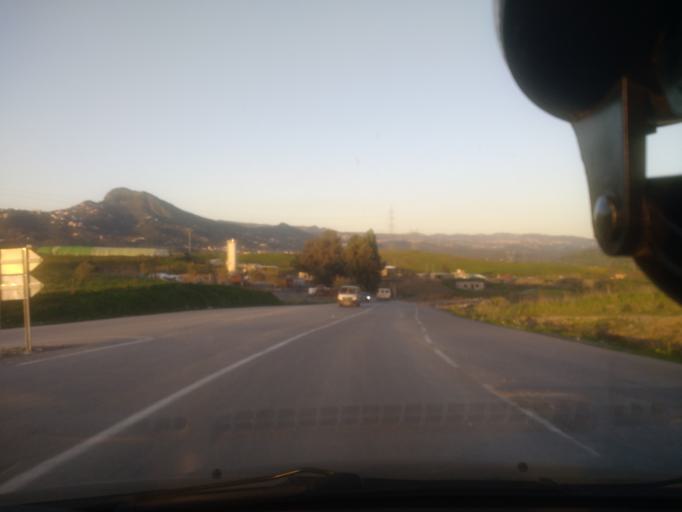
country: DZ
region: Boumerdes
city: Makouda
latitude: 36.7581
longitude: 4.0523
